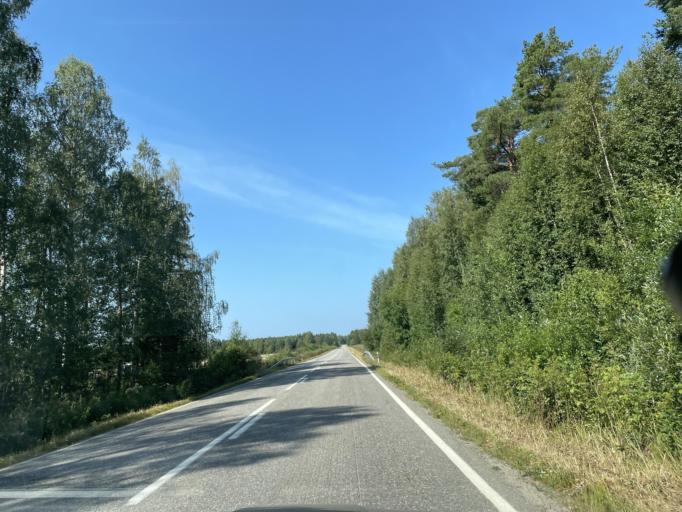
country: FI
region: Central Finland
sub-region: Saarijaervi-Viitasaari
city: Pihtipudas
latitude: 63.3640
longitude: 25.6500
